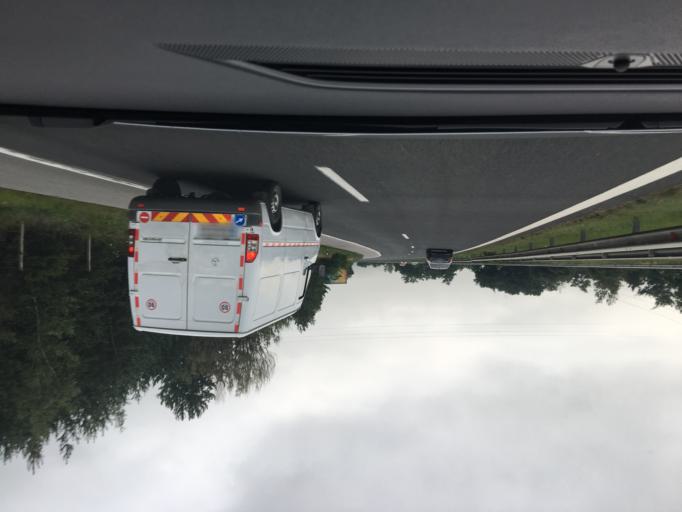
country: BG
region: Sofiya
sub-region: Obshtina Elin Pelin
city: Elin Pelin
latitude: 42.6042
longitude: 23.5598
